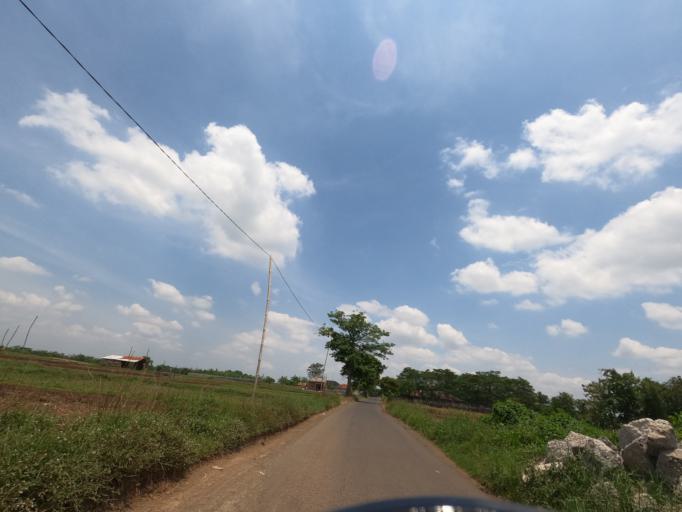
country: ID
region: West Java
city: Pamanukan
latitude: -6.5228
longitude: 107.7758
